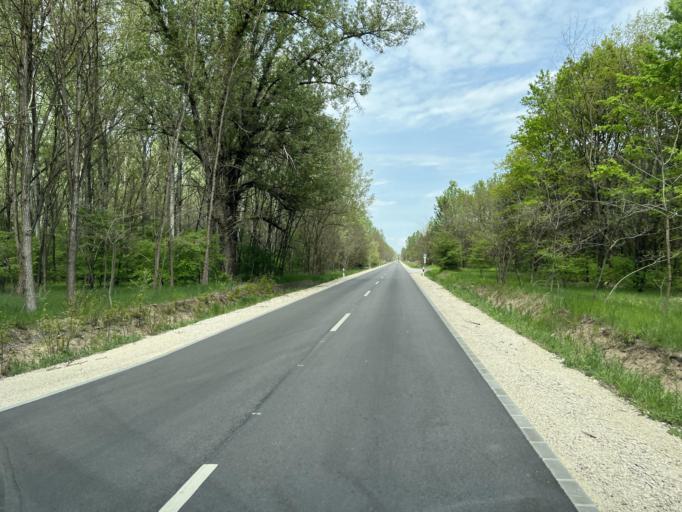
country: HU
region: Pest
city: Csemo
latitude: 47.0949
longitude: 19.6122
